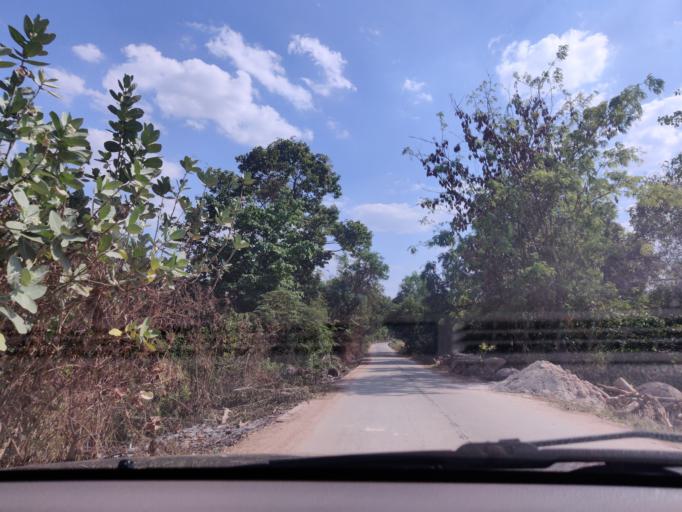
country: TH
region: Sisaket
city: Si Sa Ket
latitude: 15.0690
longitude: 104.3495
